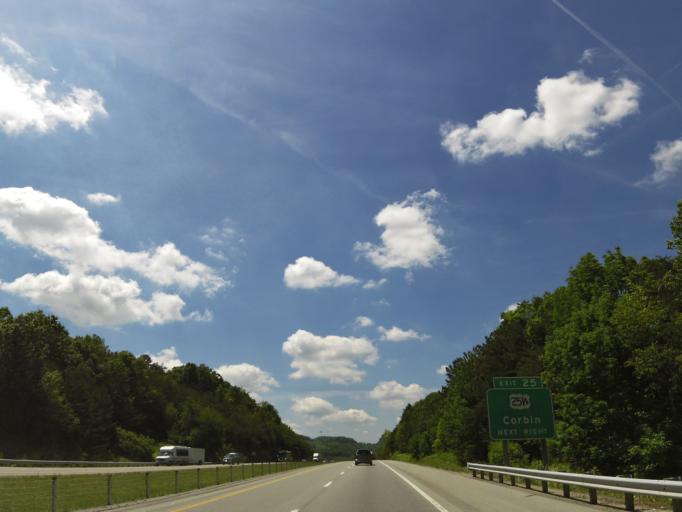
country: US
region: Kentucky
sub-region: Whitley County
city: Corbin
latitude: 36.9282
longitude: -84.1273
